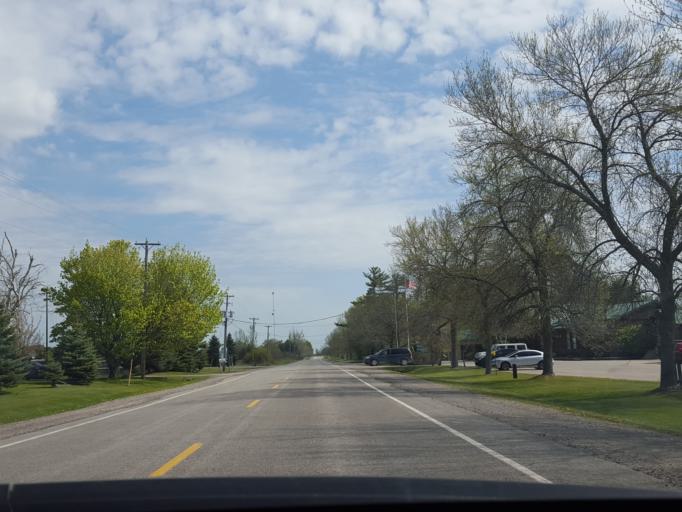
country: CA
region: Ontario
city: Uxbridge
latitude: 44.1931
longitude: -78.8816
